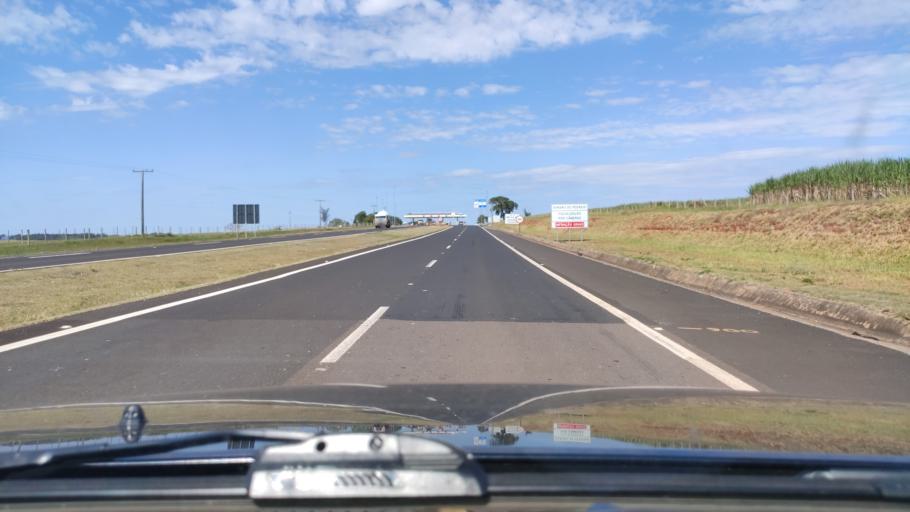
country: BR
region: Sao Paulo
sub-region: Rancharia
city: Rancharia
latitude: -22.4330
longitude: -51.0126
